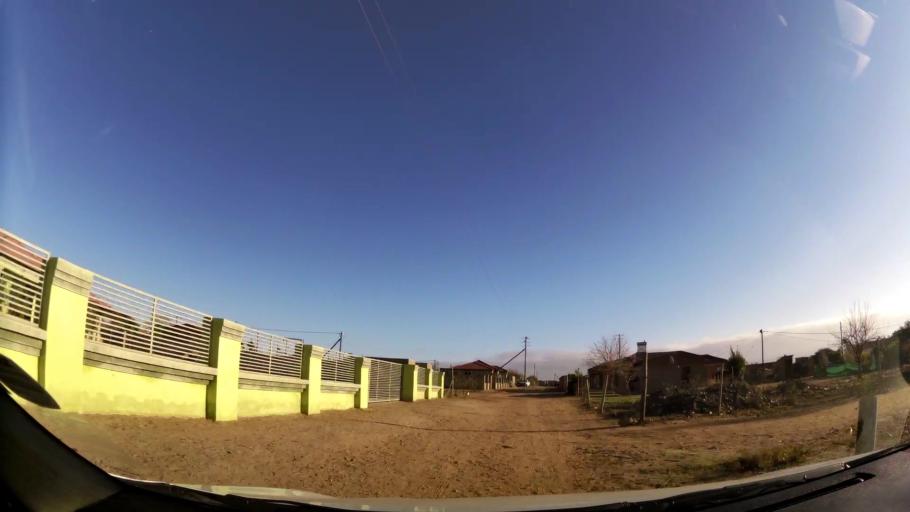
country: ZA
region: Limpopo
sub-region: Capricorn District Municipality
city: Polokwane
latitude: -23.8396
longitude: 29.3641
